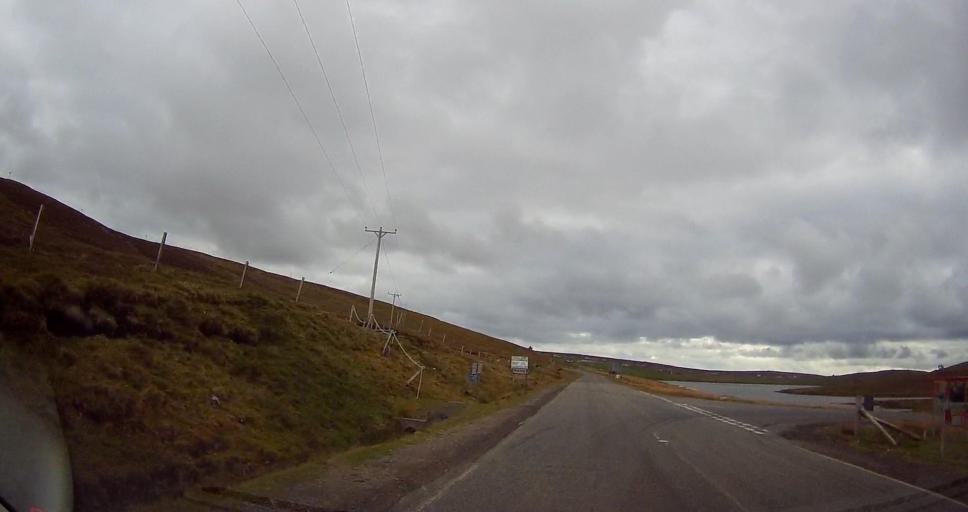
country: GB
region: Scotland
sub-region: Shetland Islands
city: Shetland
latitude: 60.6052
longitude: -1.0926
